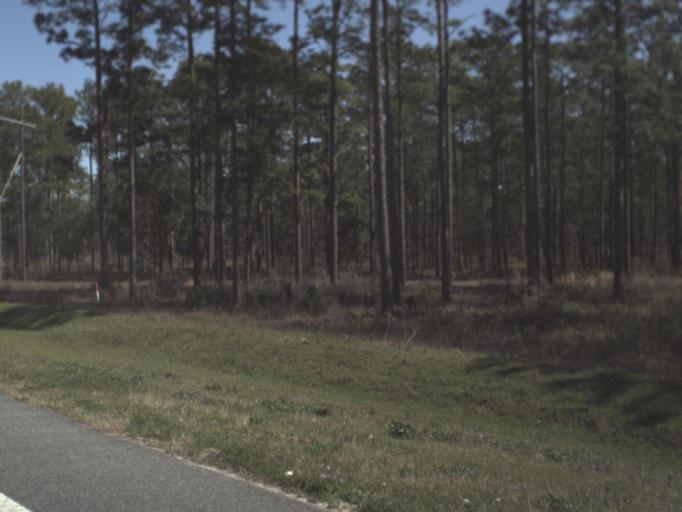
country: US
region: Florida
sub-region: Leon County
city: Woodville
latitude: 30.3471
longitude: -84.3096
